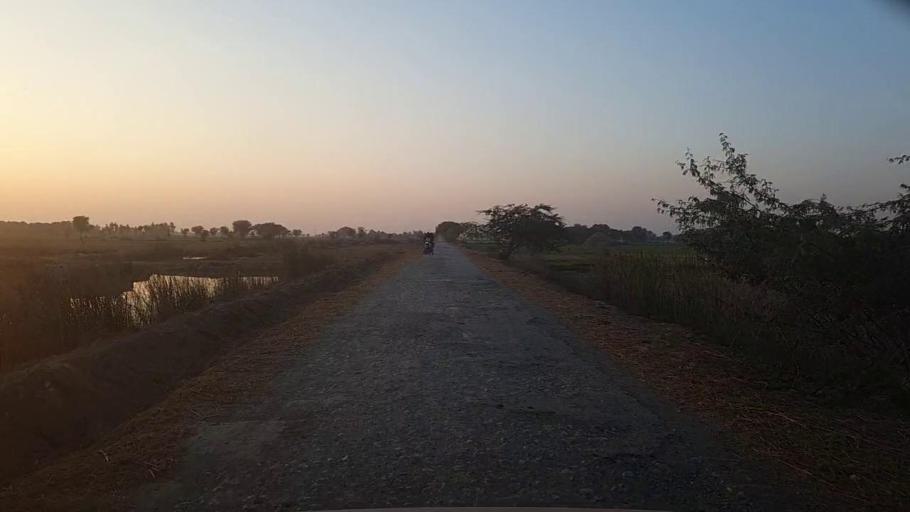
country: PK
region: Sindh
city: Khairpur Nathan Shah
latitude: 27.1561
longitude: 67.7214
